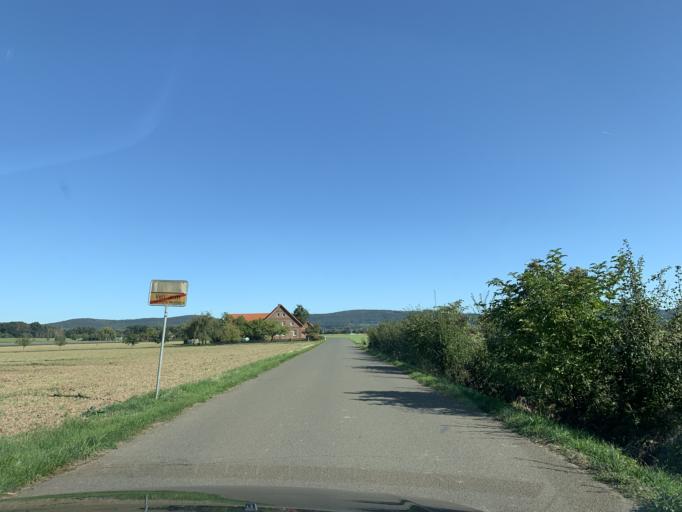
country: DE
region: North Rhine-Westphalia
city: Porta Westfalica
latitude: 52.1898
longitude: 8.9785
